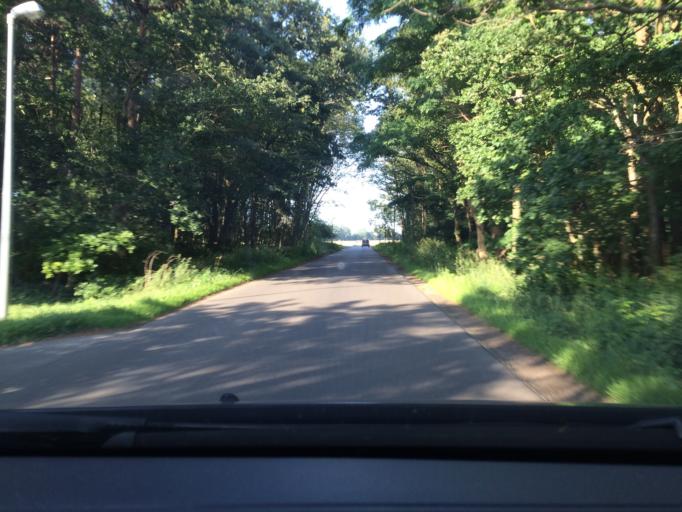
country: DE
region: Mecklenburg-Vorpommern
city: Altenpleen
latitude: 54.3555
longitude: 12.9371
